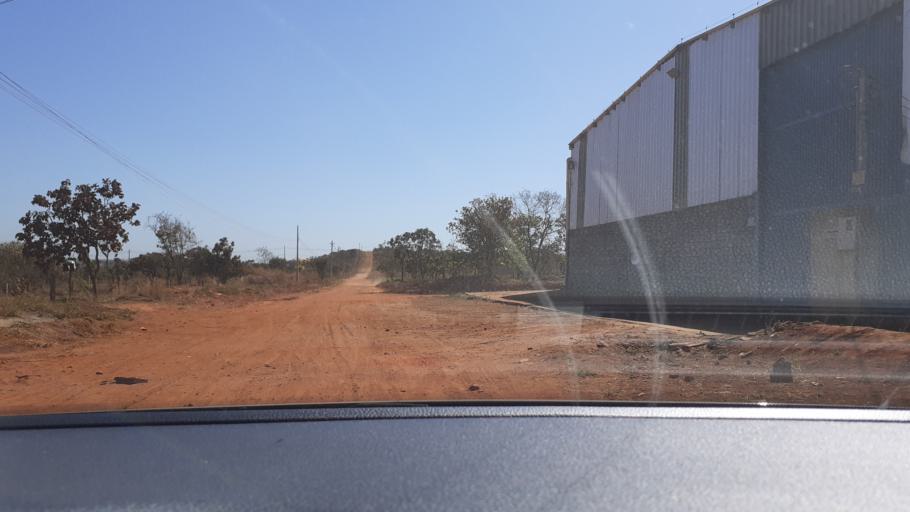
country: BR
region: Goias
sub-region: Aparecida De Goiania
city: Aparecida de Goiania
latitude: -16.8884
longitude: -49.2589
